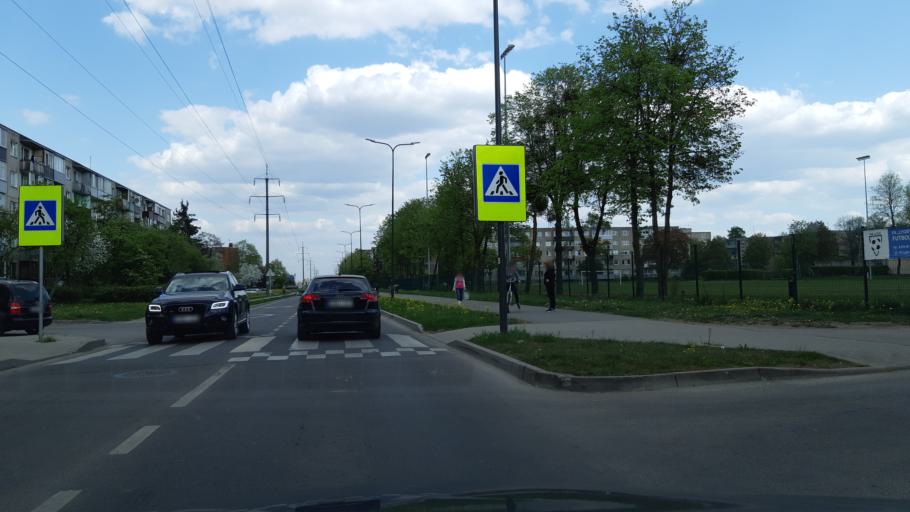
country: LT
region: Kauno apskritis
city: Dainava (Kaunas)
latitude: 54.9242
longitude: 23.9690
